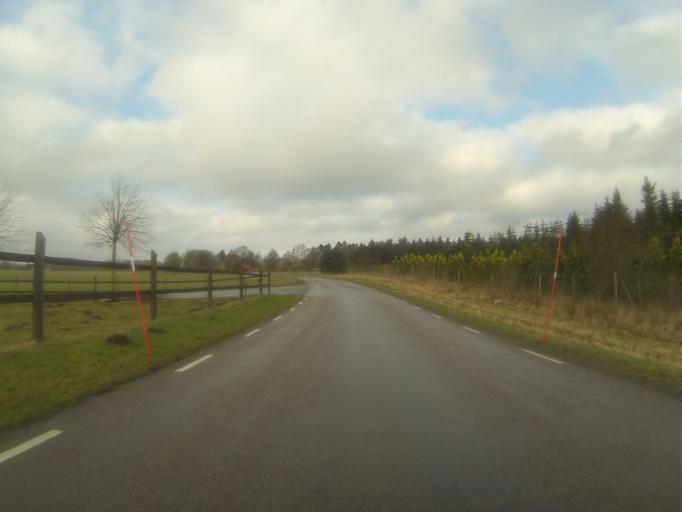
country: SE
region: Skane
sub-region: Lunds Kommun
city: Genarp
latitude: 55.5592
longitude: 13.3169
